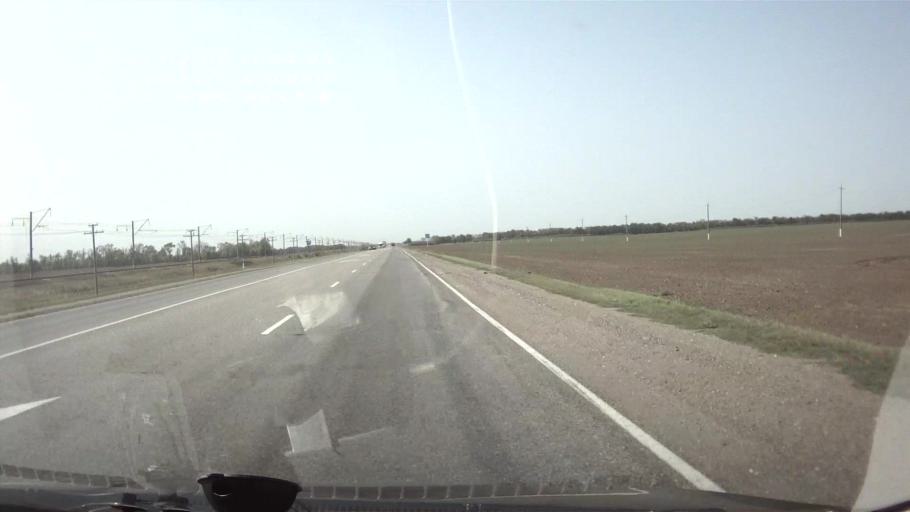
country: RU
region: Krasnodarskiy
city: Ladozhskaya
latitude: 45.3507
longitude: 40.0001
